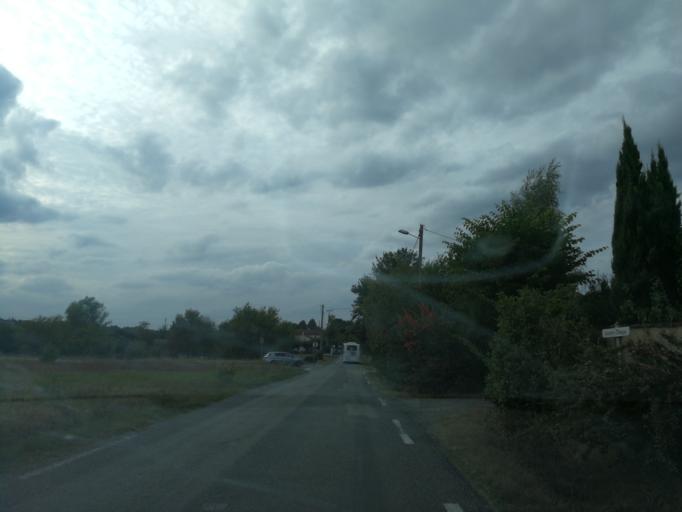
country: FR
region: Midi-Pyrenees
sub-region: Departement de la Haute-Garonne
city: Flourens
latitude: 43.5891
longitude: 1.5805
